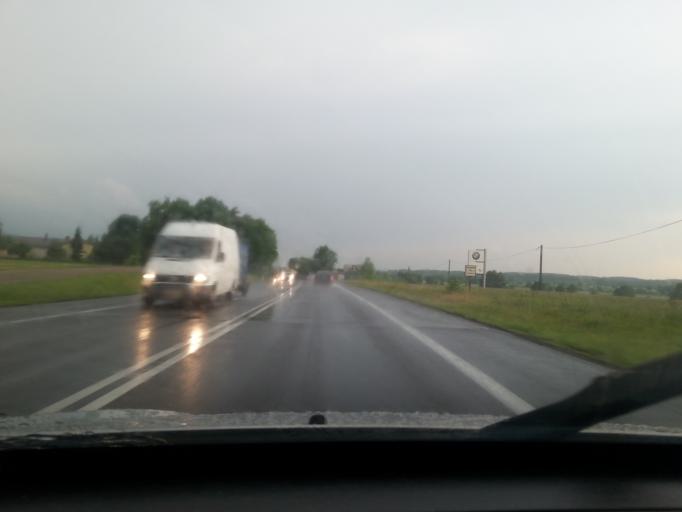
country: PL
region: Lodz Voivodeship
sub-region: Powiat zgierski
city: Strykow
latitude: 51.8665
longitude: 19.5692
